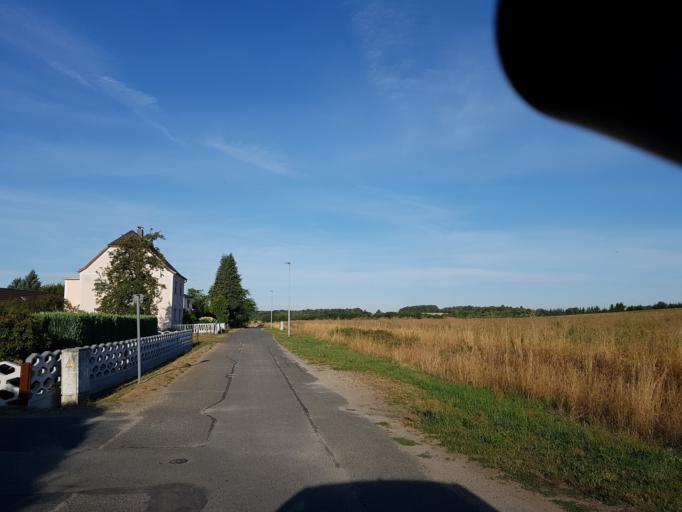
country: DE
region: Brandenburg
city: Hohenleipisch
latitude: 51.4944
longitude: 13.5462
